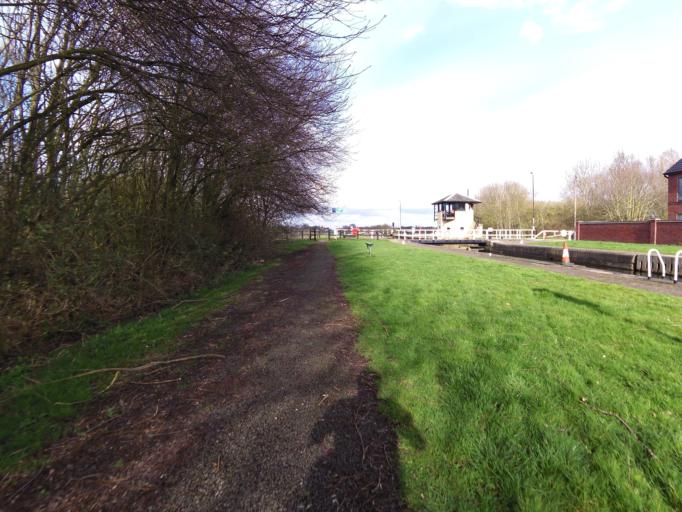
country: GB
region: England
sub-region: Doncaster
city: Stainforth
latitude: 53.6372
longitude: -1.0363
